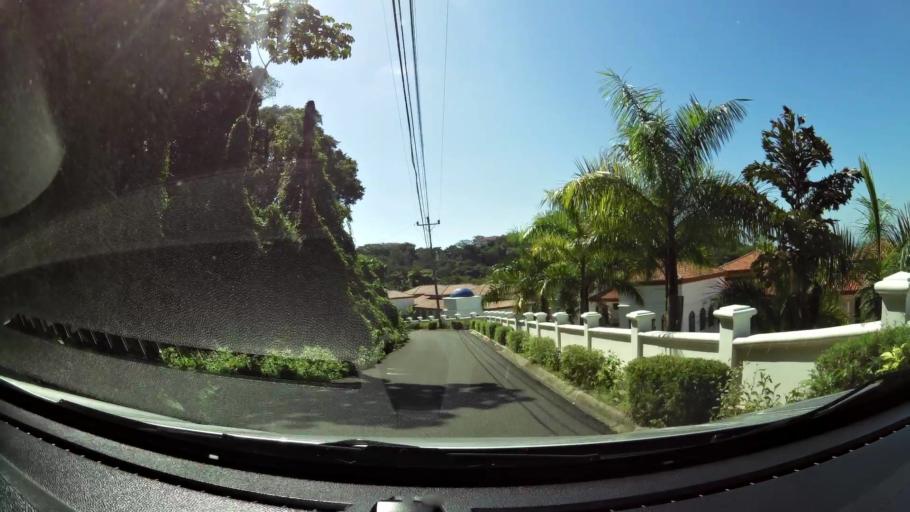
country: CR
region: Puntarenas
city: Quepos
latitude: 9.4002
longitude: -84.1652
